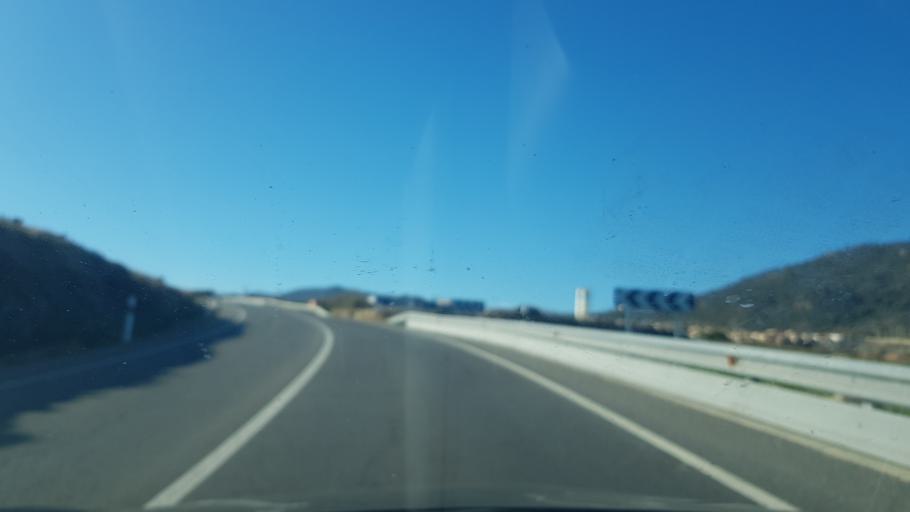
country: ES
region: Castille and Leon
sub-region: Provincia de Avila
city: Barraco
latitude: 40.4724
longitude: -4.6320
